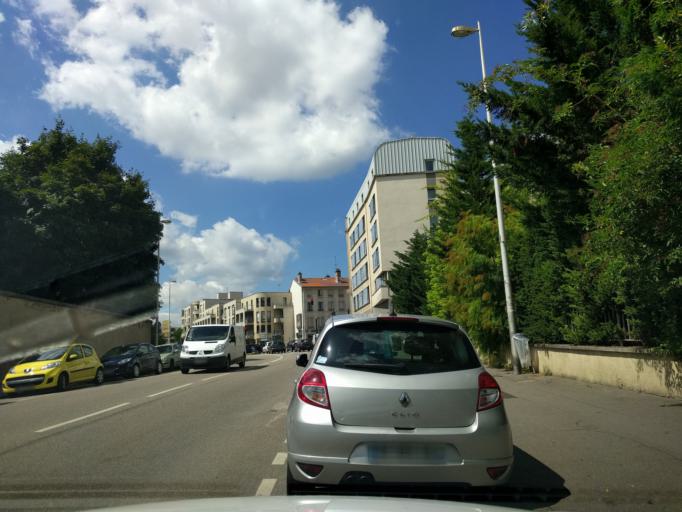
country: FR
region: Lorraine
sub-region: Departement de Meurthe-et-Moselle
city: Nancy
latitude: 48.6848
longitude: 6.1894
